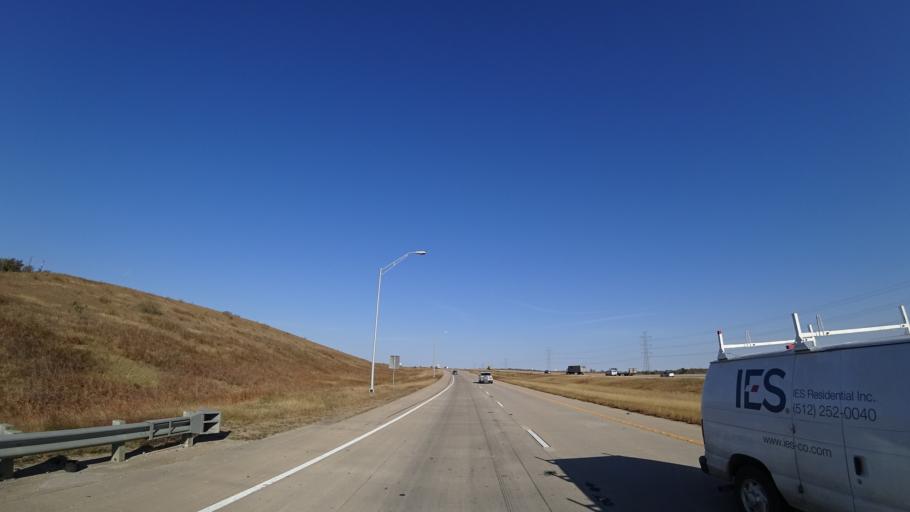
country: US
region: Texas
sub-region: Travis County
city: Manor
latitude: 30.3095
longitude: -97.5706
